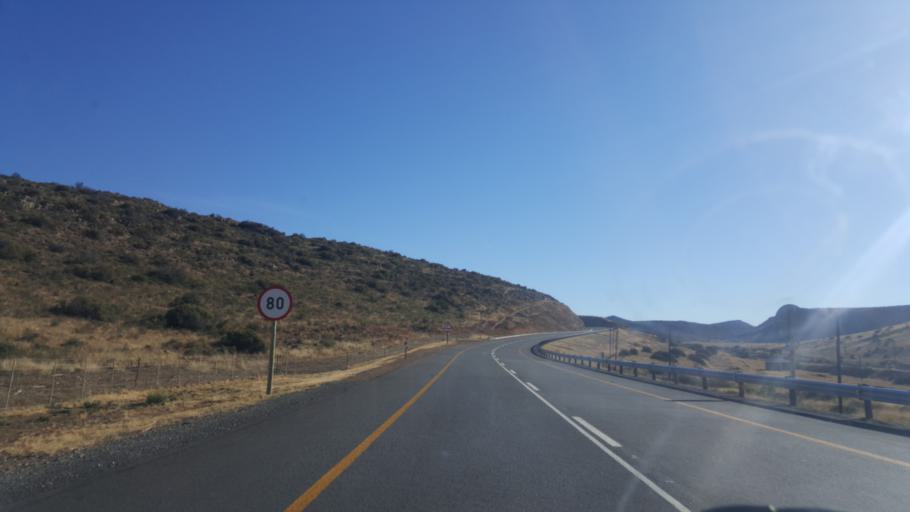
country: ZA
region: Eastern Cape
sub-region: Chris Hani District Municipality
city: Middelburg
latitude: -31.3840
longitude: 25.0321
